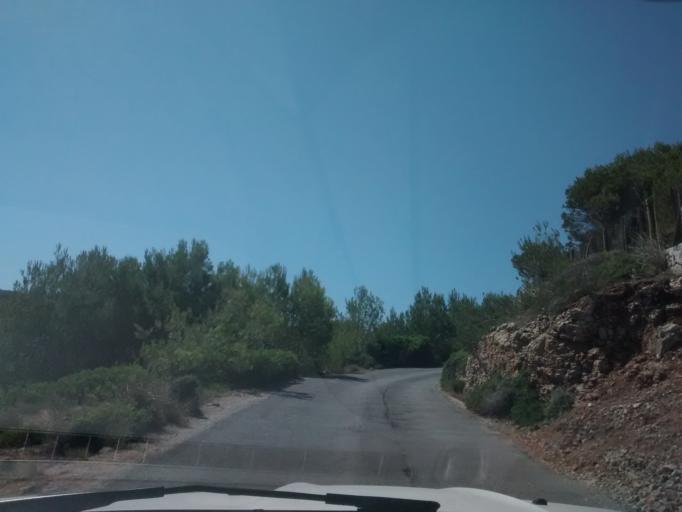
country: ES
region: Balearic Islands
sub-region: Illes Balears
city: Port d'Alcudia
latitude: 39.8711
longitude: 3.1530
